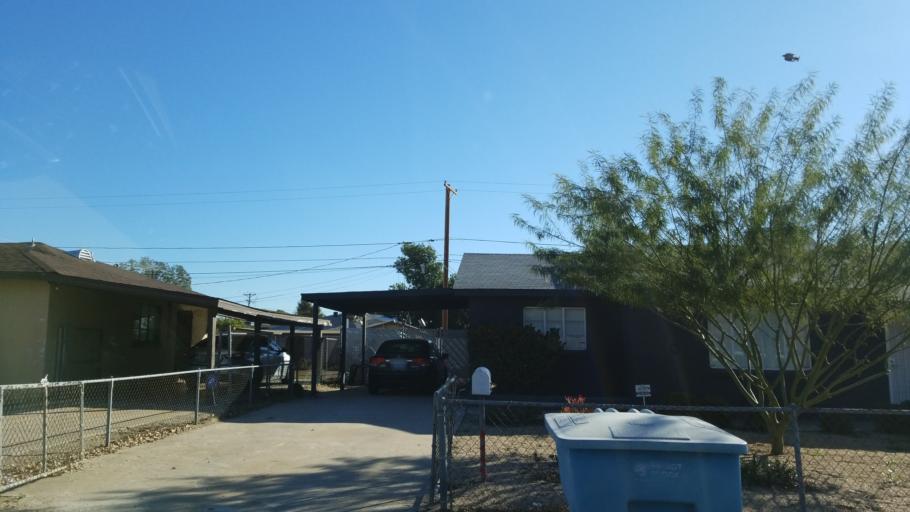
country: US
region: Arizona
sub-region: Maricopa County
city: Glendale
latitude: 33.5635
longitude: -112.1255
